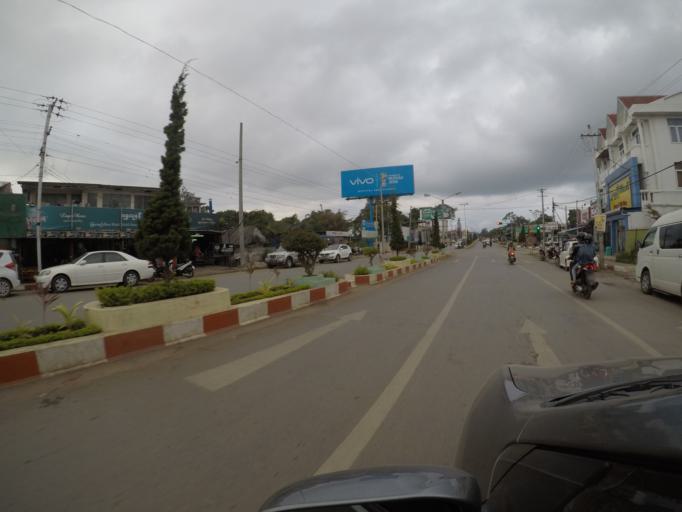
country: MM
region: Shan
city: Taunggyi
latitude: 20.7973
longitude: 97.0370
